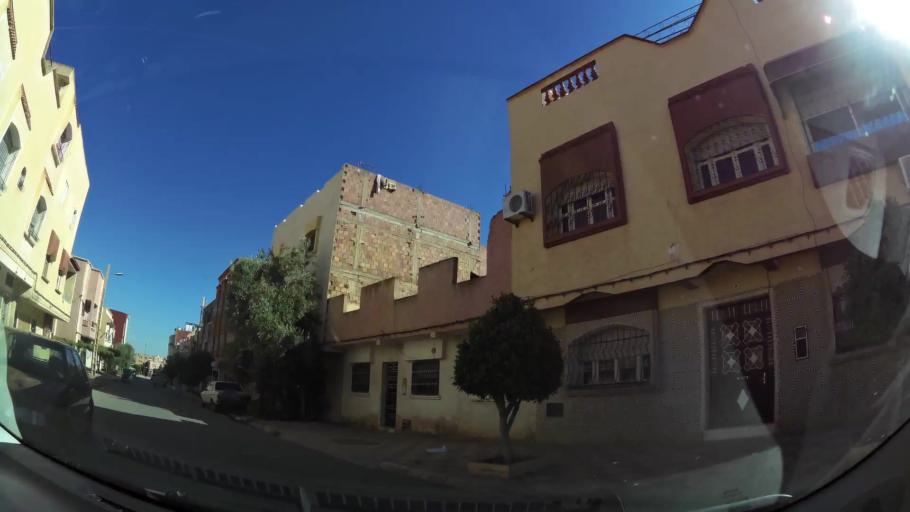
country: MA
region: Oriental
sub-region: Oujda-Angad
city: Oujda
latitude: 34.6530
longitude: -1.8938
